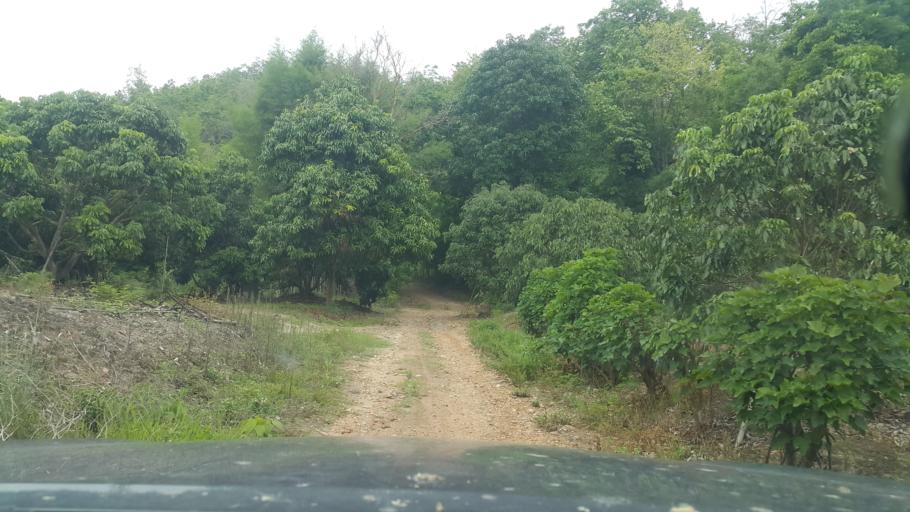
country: TH
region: Chiang Mai
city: Hang Dong
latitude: 18.6855
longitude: 98.8424
